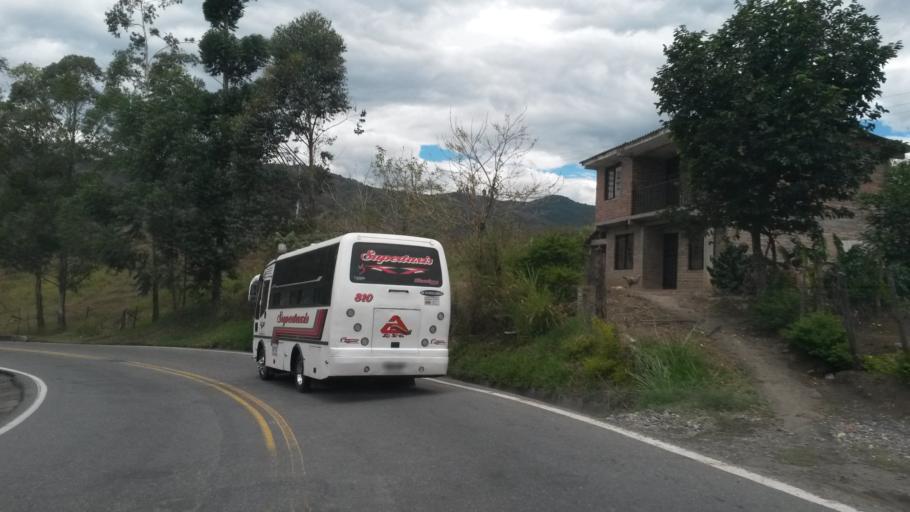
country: CO
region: Cauca
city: Rosas
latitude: 2.2801
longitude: -76.7221
